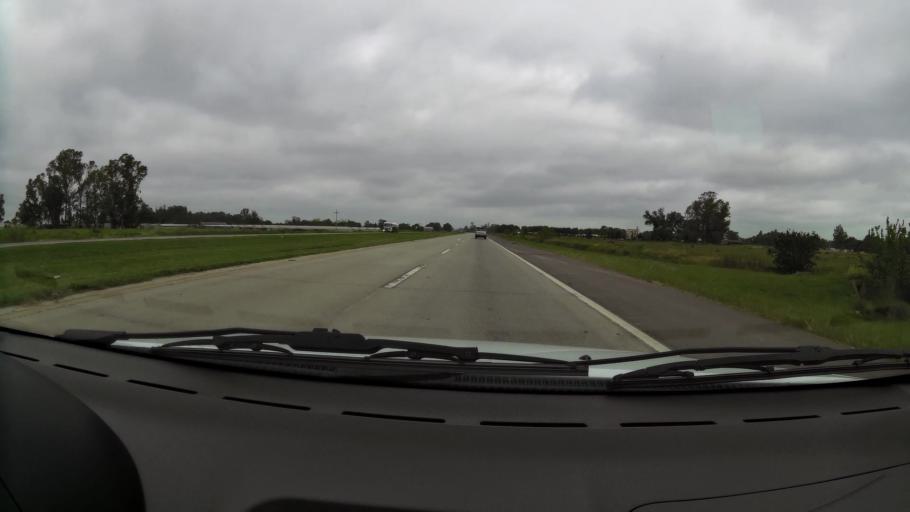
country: AR
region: Buenos Aires
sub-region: Partido de Brandsen
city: Brandsen
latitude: -35.0496
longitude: -58.1224
